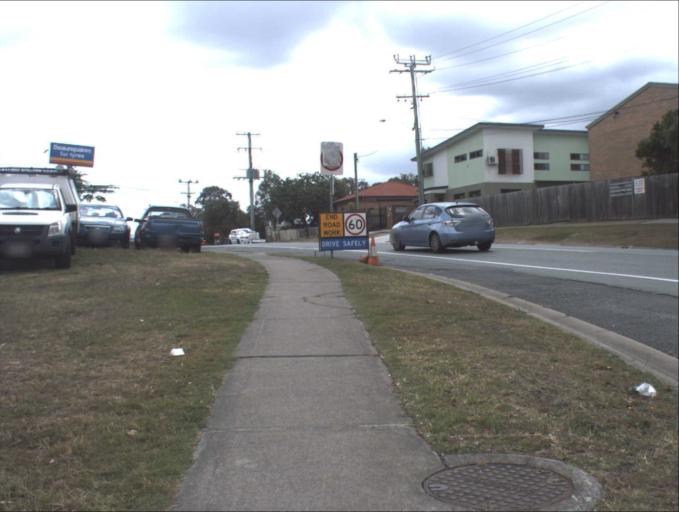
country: AU
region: Queensland
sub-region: Logan
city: Beenleigh
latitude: -27.7136
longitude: 153.1941
